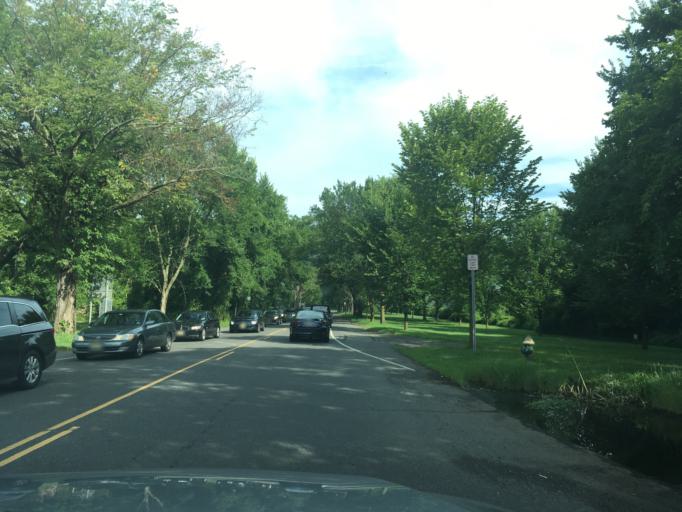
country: US
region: New Jersey
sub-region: Mercer County
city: Princeton Junction
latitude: 40.3319
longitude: -74.6384
